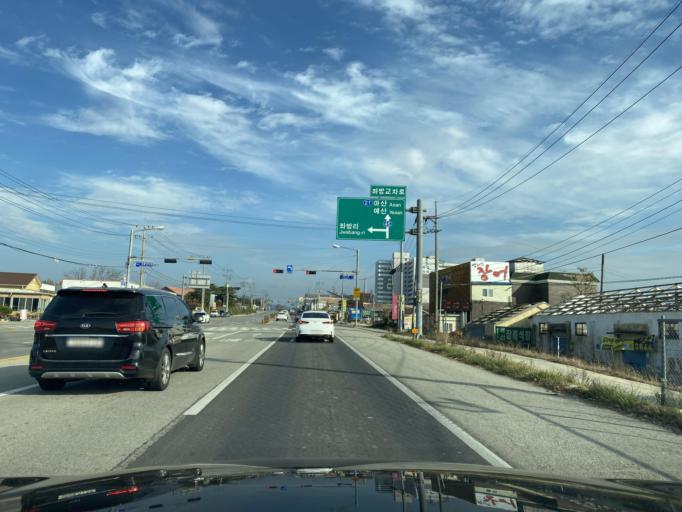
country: KR
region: Chungcheongnam-do
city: Yesan
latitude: 36.6860
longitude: 126.7733
